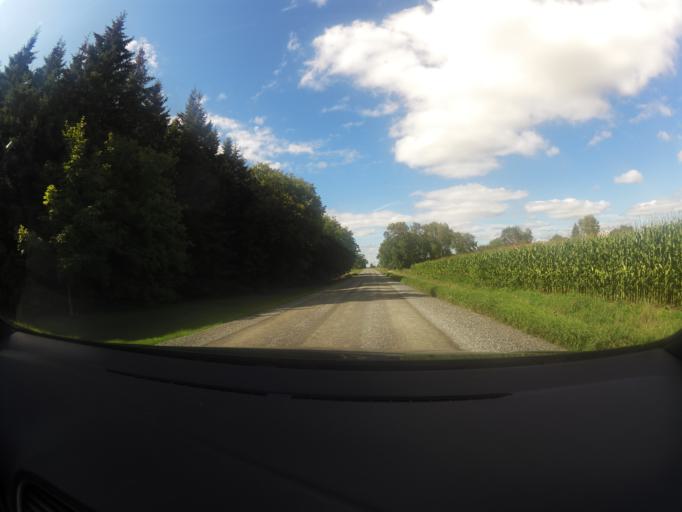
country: CA
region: Ontario
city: Carleton Place
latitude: 45.2832
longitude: -76.1675
